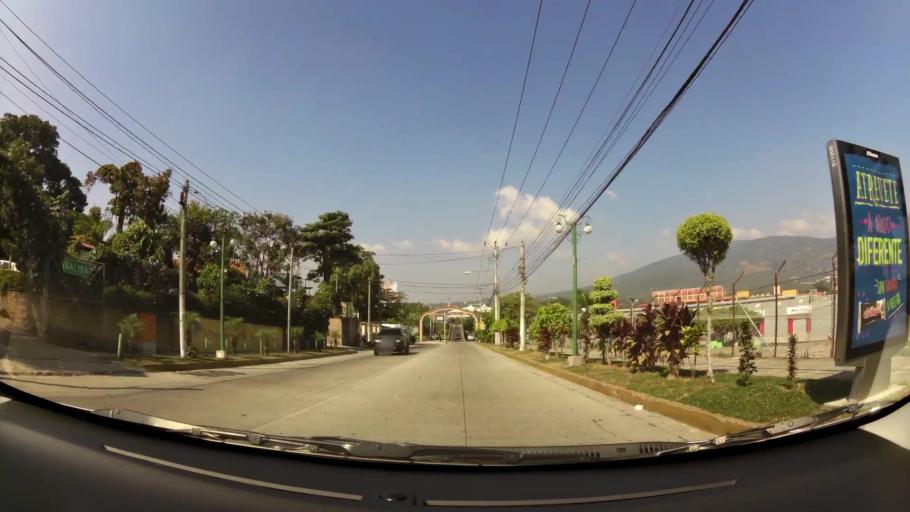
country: SV
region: La Libertad
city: Antiguo Cuscatlan
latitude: 13.6764
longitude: -89.2461
